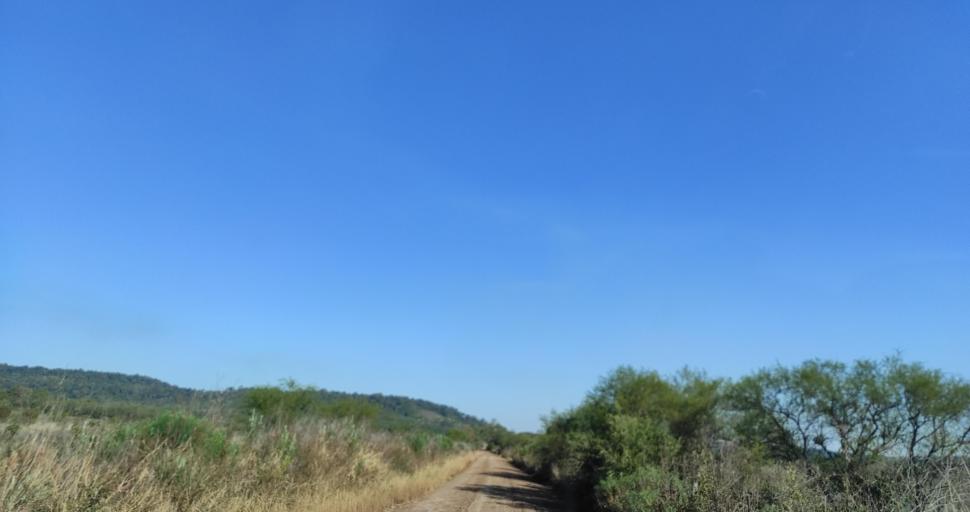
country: AR
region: Misiones
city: Cerro Cora
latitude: -27.6573
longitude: -55.6587
